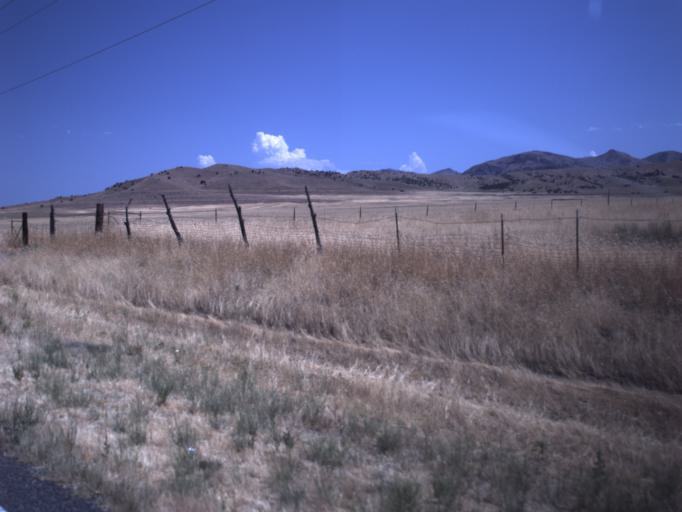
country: US
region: Utah
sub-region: Millard County
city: Delta
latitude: 39.4212
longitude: -112.3280
